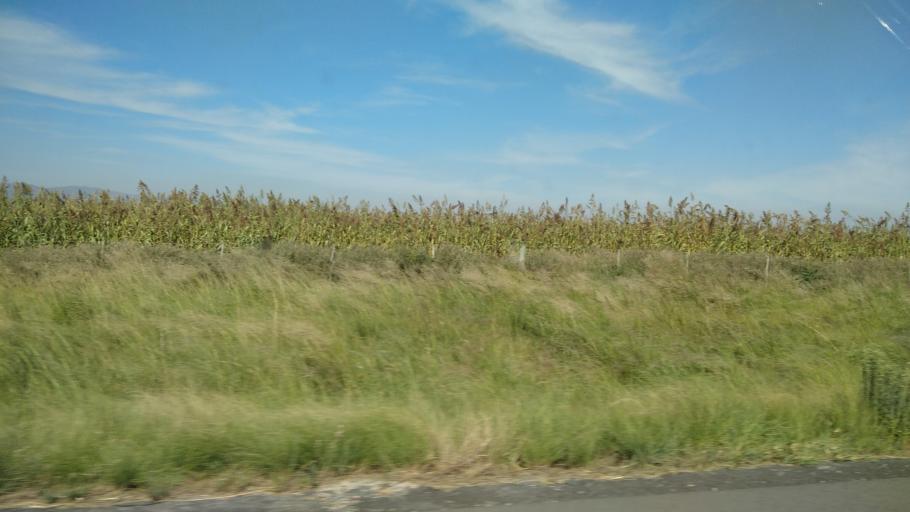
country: ZA
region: Western Cape
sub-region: West Coast District Municipality
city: Malmesbury
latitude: -33.5521
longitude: 18.6316
